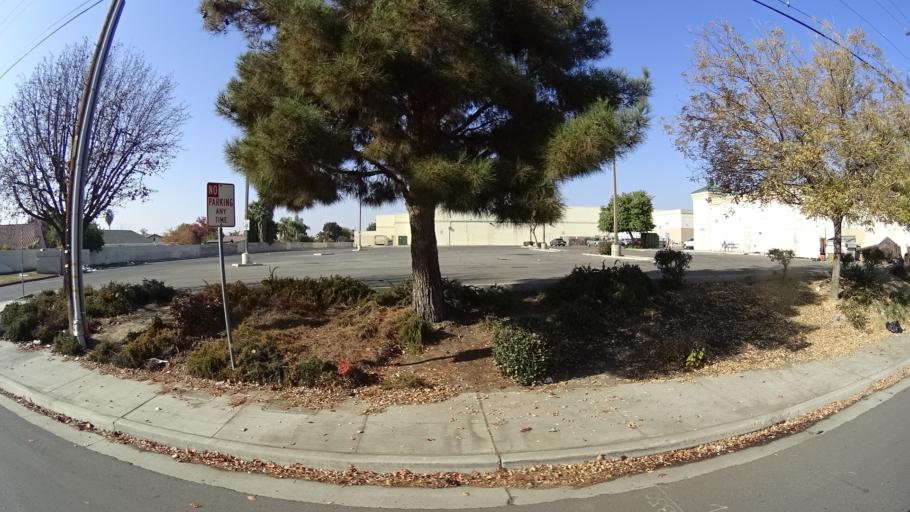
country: US
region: California
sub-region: Kern County
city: Greenfield
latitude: 35.3158
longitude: -119.0214
